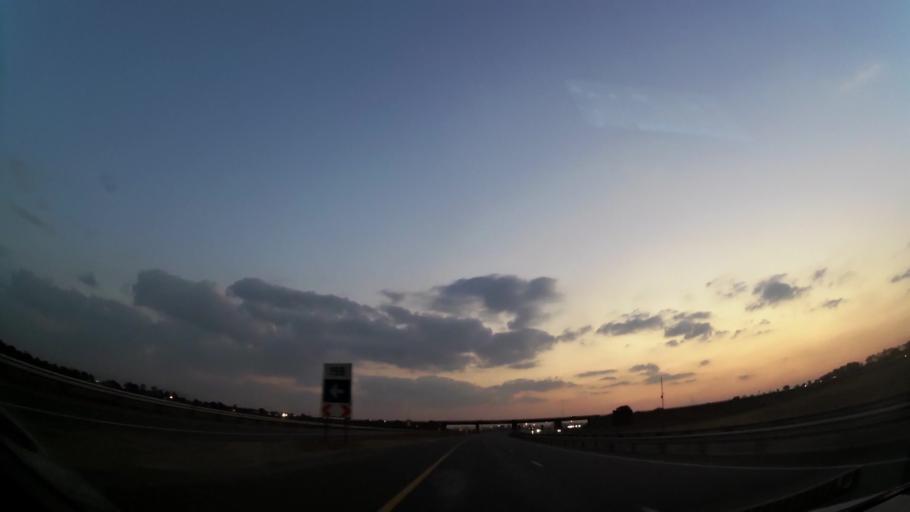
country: ZA
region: Gauteng
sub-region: Ekurhuleni Metropolitan Municipality
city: Springs
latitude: -26.2847
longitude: 28.4321
